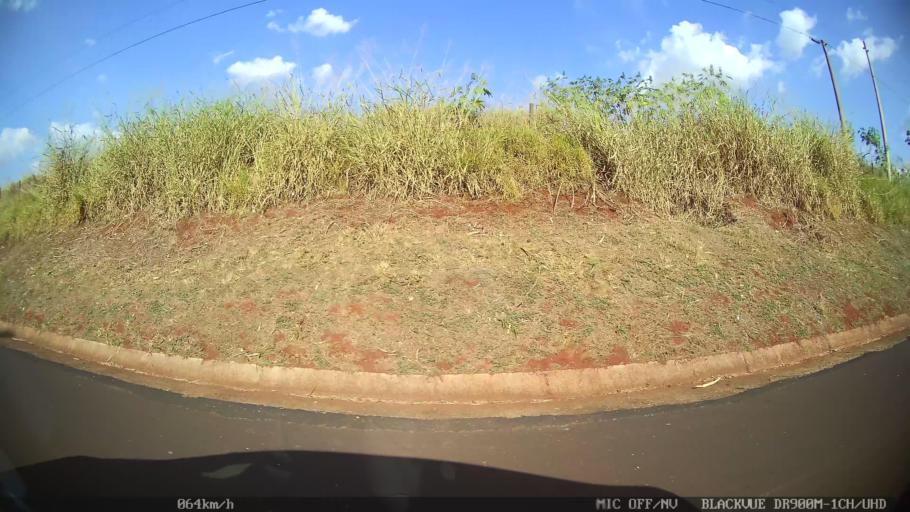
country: BR
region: Sao Paulo
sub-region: Ribeirao Preto
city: Ribeirao Preto
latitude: -21.1950
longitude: -47.8721
